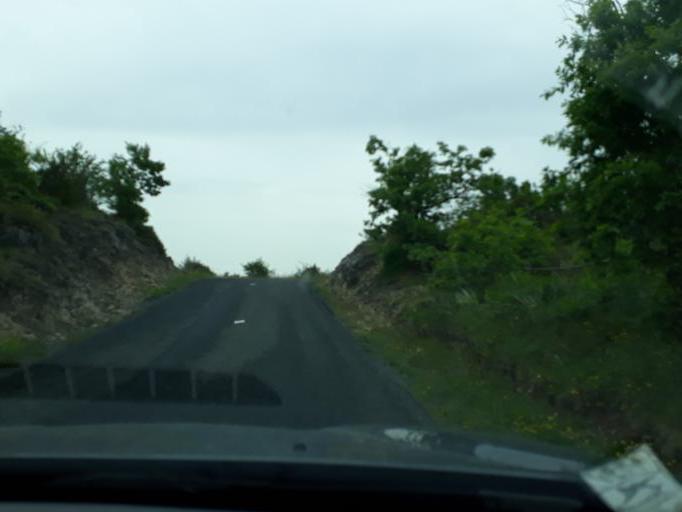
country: FR
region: Languedoc-Roussillon
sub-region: Departement de l'Herault
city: Lodeve
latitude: 43.8117
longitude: 3.2693
